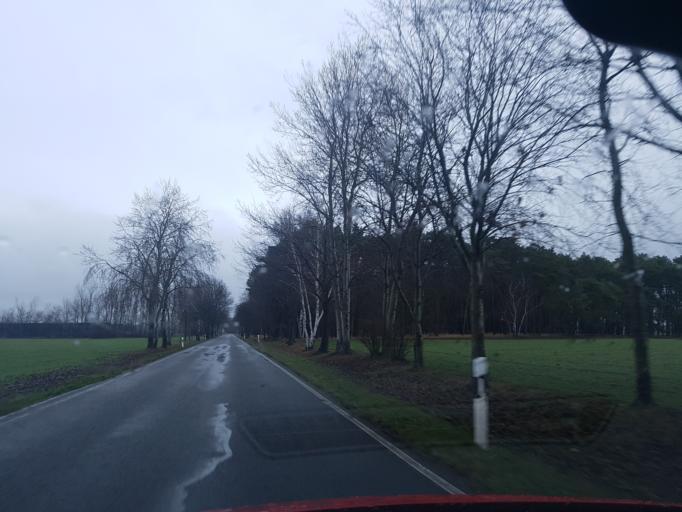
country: DE
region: Brandenburg
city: Schilda
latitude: 51.6150
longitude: 13.3188
